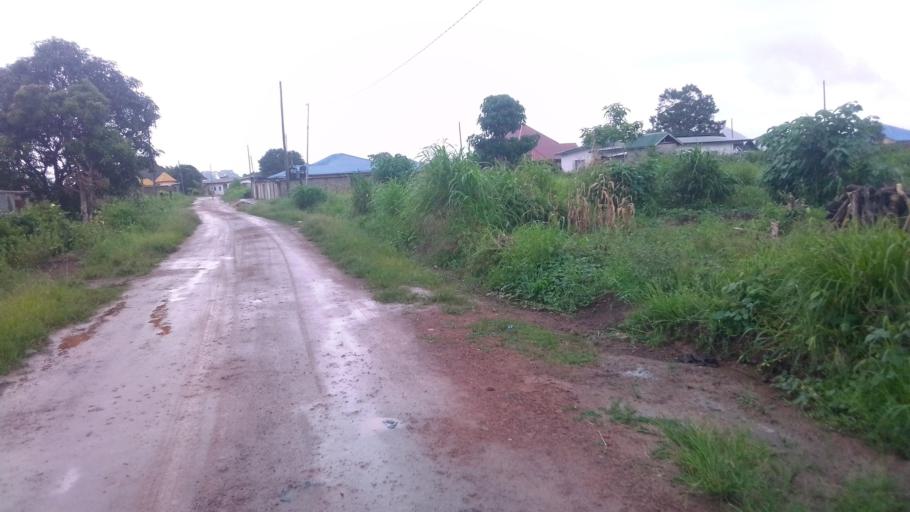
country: SL
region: Eastern Province
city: Hangha
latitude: 7.9112
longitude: -11.1639
